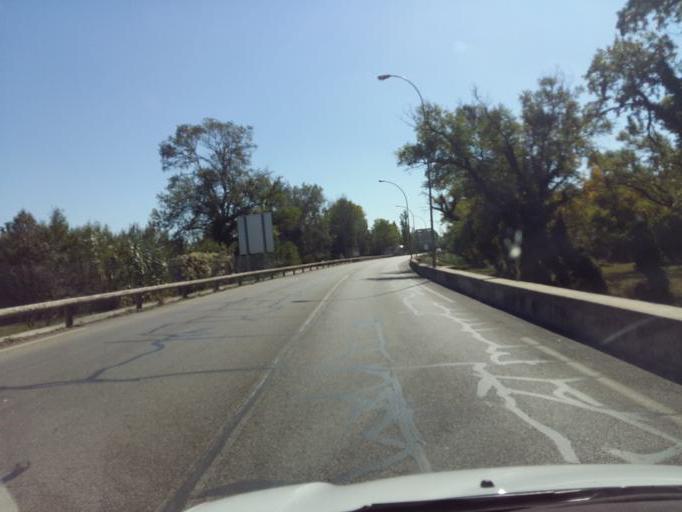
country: FR
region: Provence-Alpes-Cote d'Azur
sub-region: Departement du Vaucluse
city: Cavaillon
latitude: 43.8261
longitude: 5.0355
